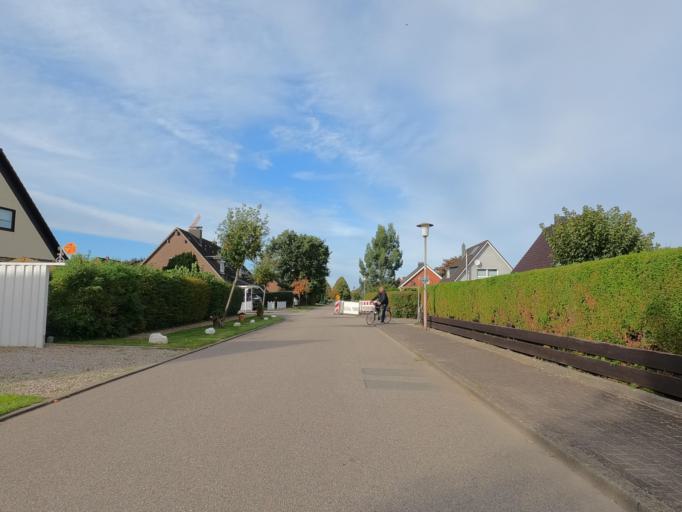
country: DE
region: Schleswig-Holstein
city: Grube
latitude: 54.2270
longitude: 11.0383
